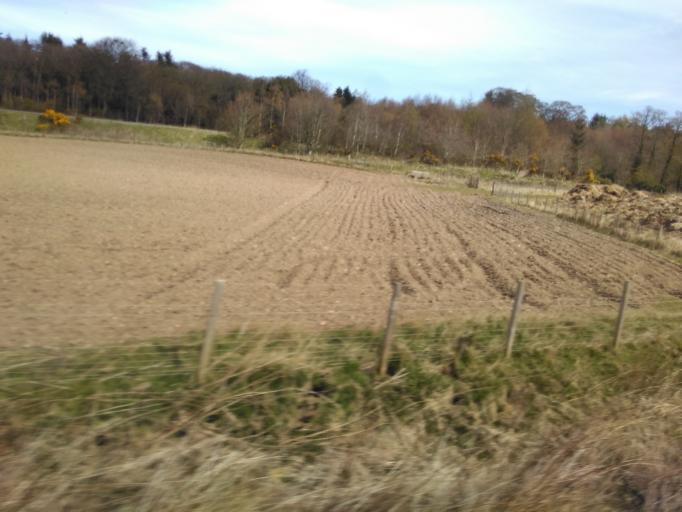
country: GB
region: Scotland
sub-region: The Scottish Borders
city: Chirnside
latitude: 55.8572
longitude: -2.2375
